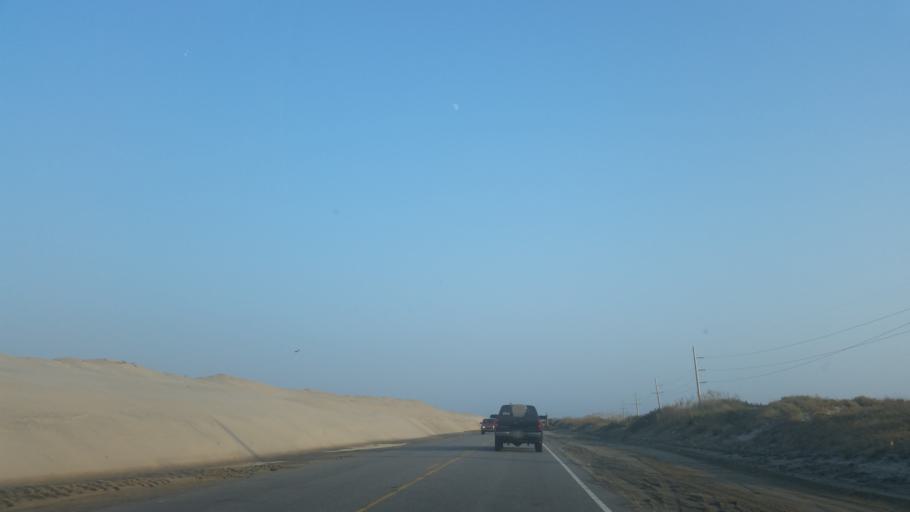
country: US
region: North Carolina
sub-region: Dare County
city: Wanchese
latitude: 35.7624
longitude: -75.5177
